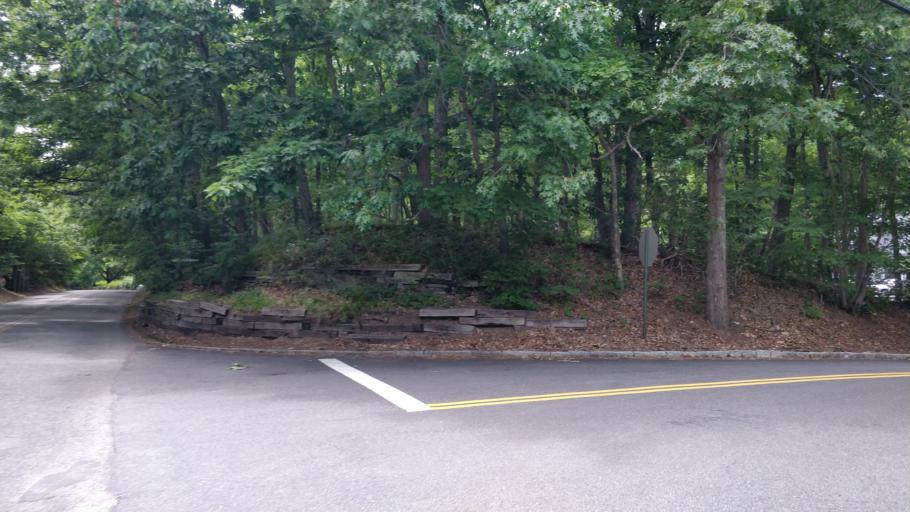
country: US
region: New York
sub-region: Nassau County
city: Woodbury
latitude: 40.8411
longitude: -73.4651
